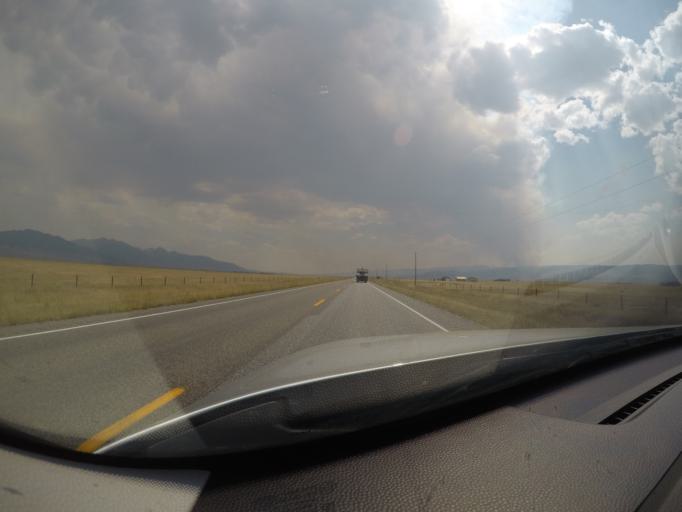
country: US
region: Montana
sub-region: Madison County
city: Virginia City
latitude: 45.1853
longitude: -111.6789
